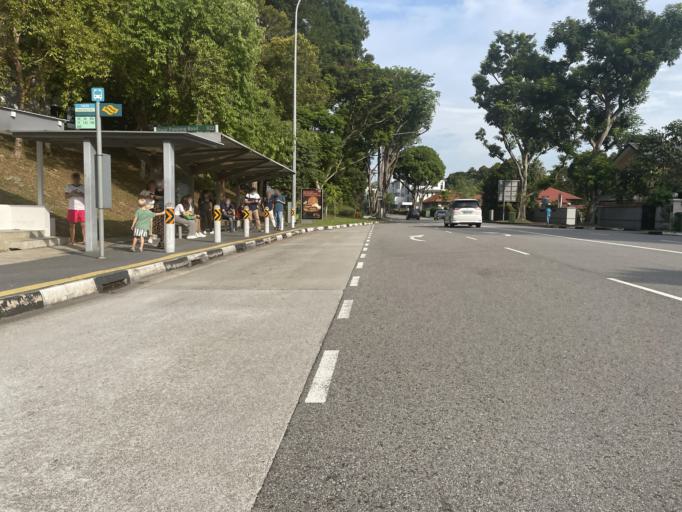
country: SG
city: Singapore
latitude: 1.2879
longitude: 103.7787
